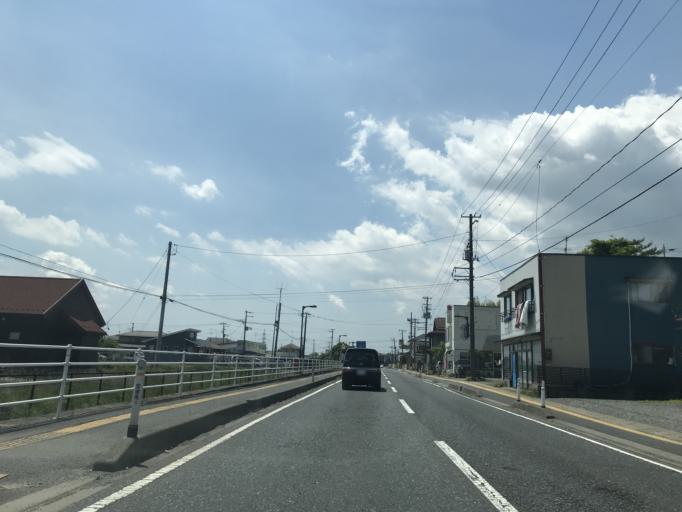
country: JP
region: Miyagi
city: Wakuya
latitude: 38.4697
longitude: 141.0946
